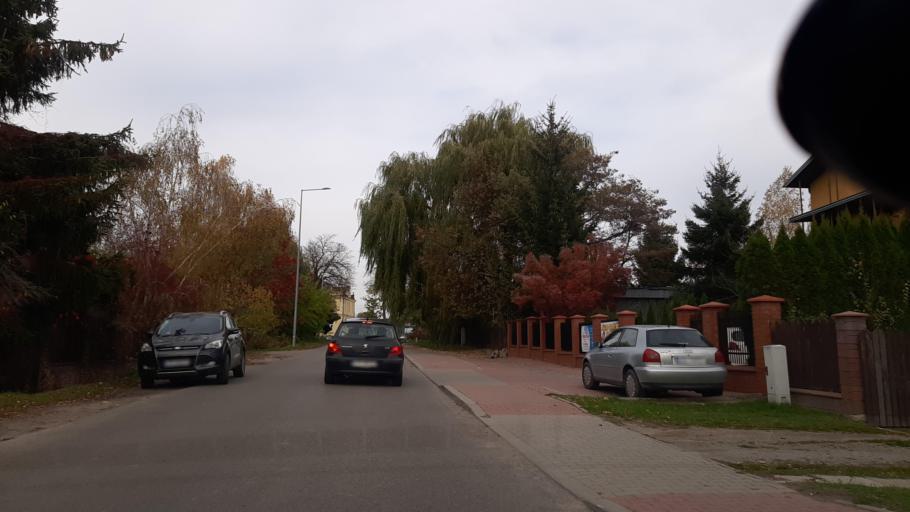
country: PL
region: Lublin Voivodeship
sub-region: Powiat pulawski
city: Naleczow
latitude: 51.3164
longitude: 22.2134
